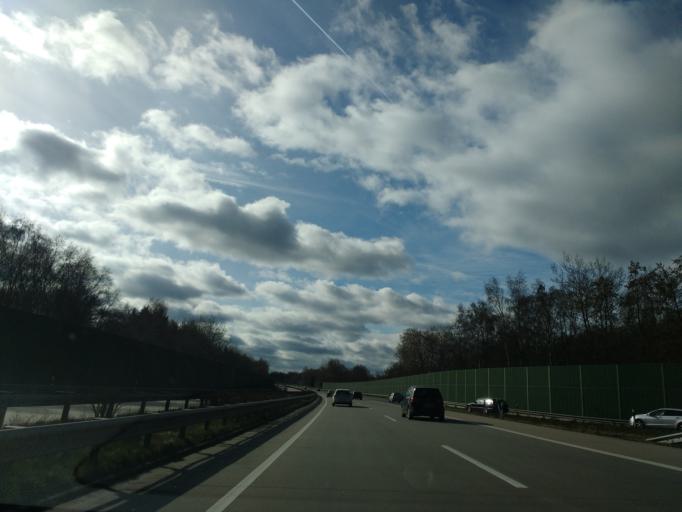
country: DE
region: Lower Saxony
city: Langen
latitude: 53.5789
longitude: 8.6212
